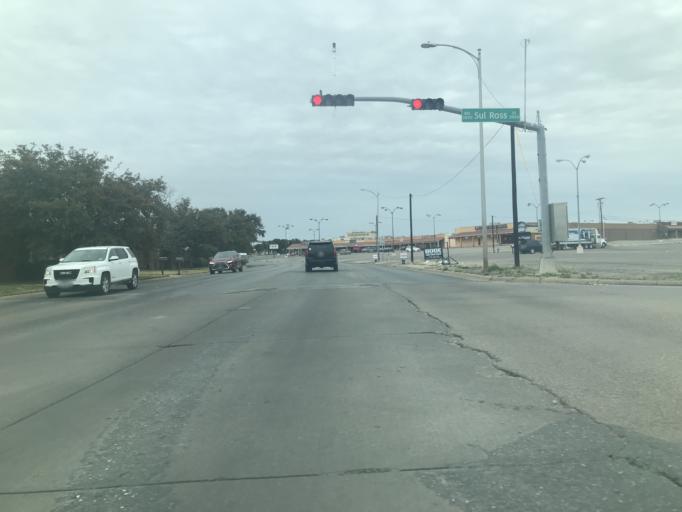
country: US
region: Texas
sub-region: Tom Green County
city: San Angelo
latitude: 31.4220
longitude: -100.4749
